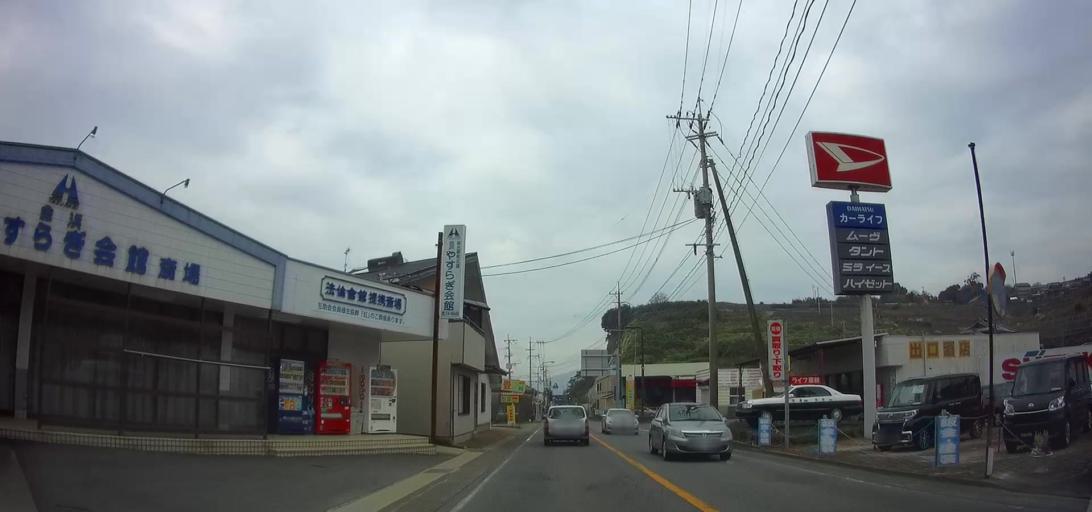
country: JP
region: Nagasaki
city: Shimabara
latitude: 32.7097
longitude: 130.1883
